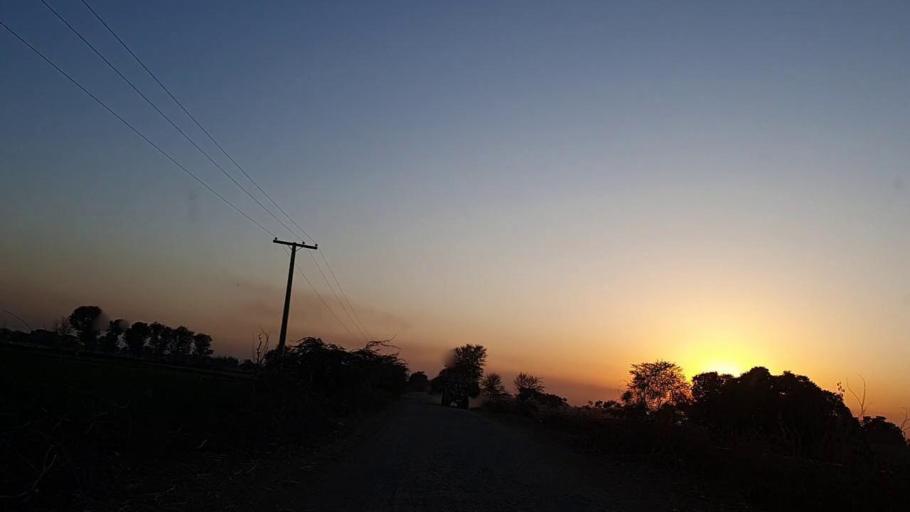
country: PK
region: Sindh
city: Daur
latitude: 26.3444
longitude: 68.3026
